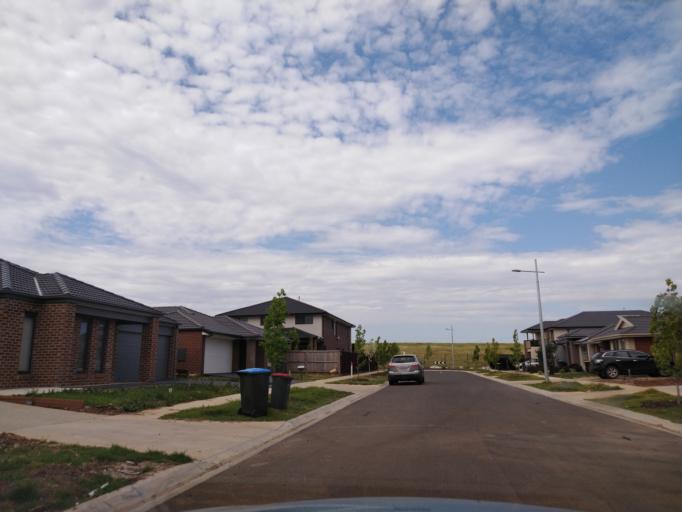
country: AU
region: Victoria
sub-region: Wyndham
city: Williams Landing
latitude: -37.8489
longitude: 144.7159
